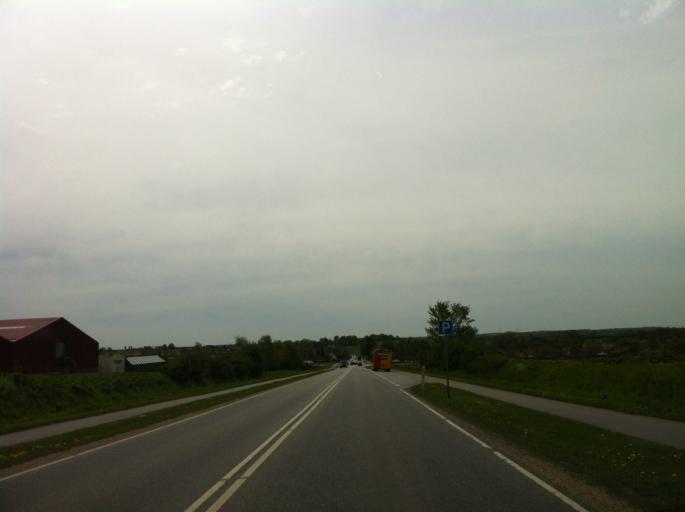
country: DK
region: Zealand
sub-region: Ringsted Kommune
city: Ringsted
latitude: 55.4270
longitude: 11.7875
